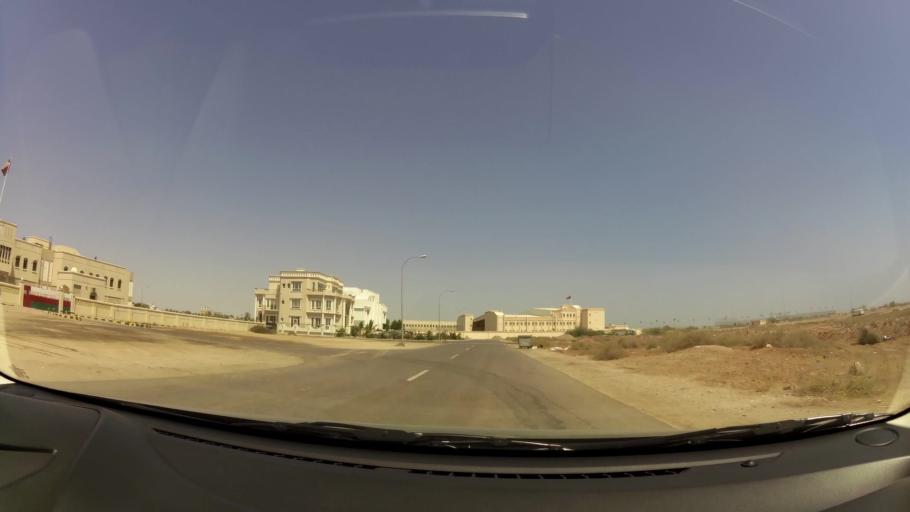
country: OM
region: Muhafazat Masqat
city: As Sib al Jadidah
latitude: 23.6282
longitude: 58.2533
